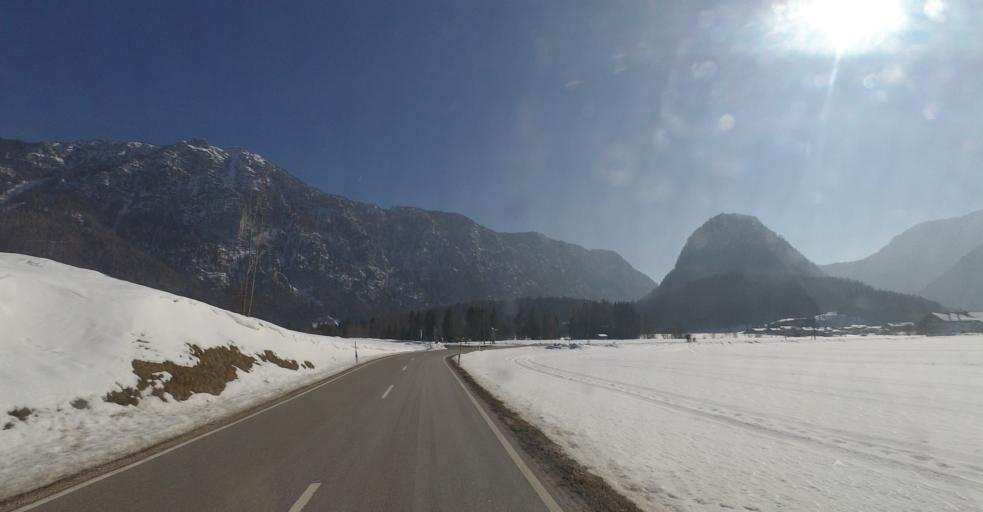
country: DE
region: Bavaria
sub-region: Upper Bavaria
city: Inzell
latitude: 47.7653
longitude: 12.7654
